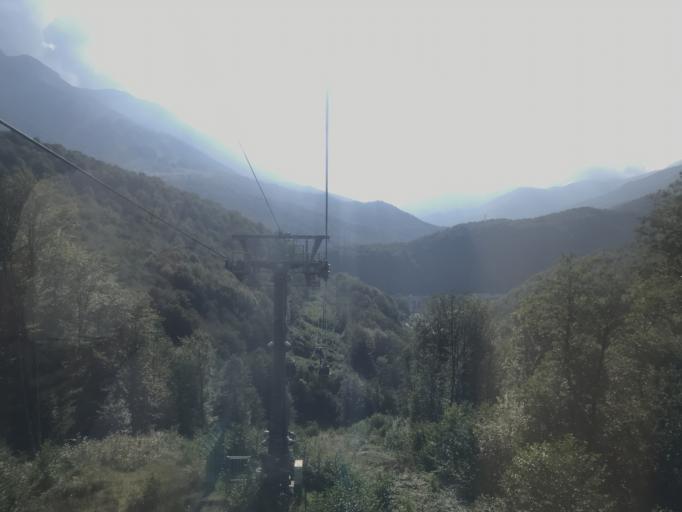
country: RU
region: Krasnodarskiy
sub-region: Sochi City
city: Krasnaya Polyana
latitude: 43.6880
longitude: 40.2943
